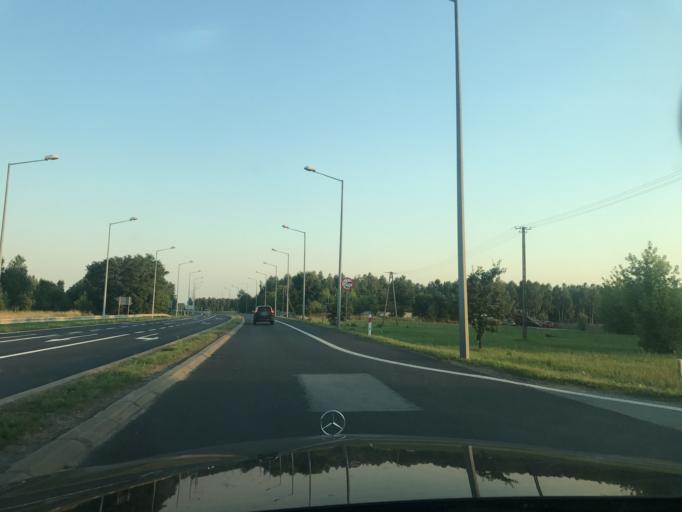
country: PL
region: Lublin Voivodeship
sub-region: Powiat lubartowski
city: Lubartow
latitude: 51.4628
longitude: 22.5764
